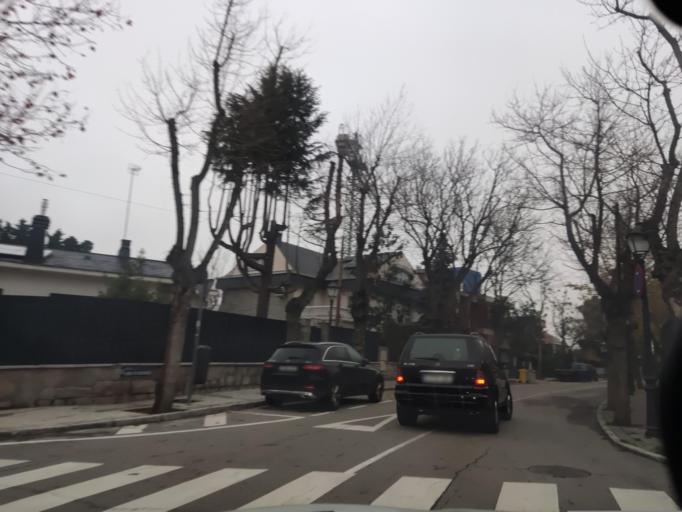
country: ES
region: Madrid
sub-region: Provincia de Madrid
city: Tetuan de las Victorias
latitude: 40.4886
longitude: -3.7101
